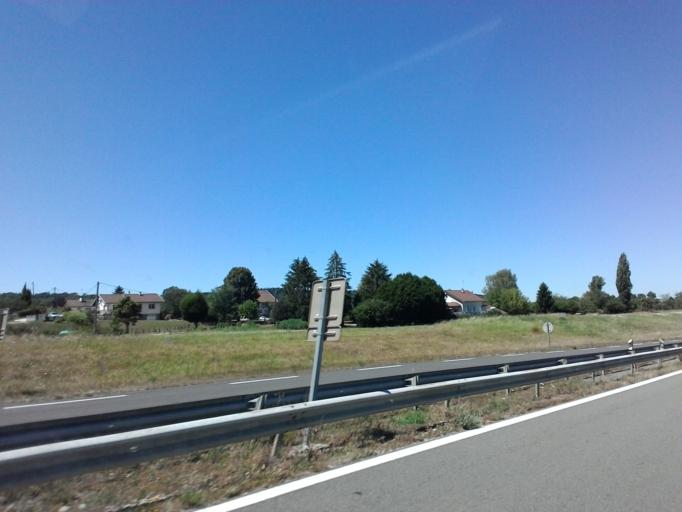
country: FR
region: Franche-Comte
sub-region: Departement du Jura
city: Lons-le-Saunier
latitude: 46.7246
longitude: 5.5576
